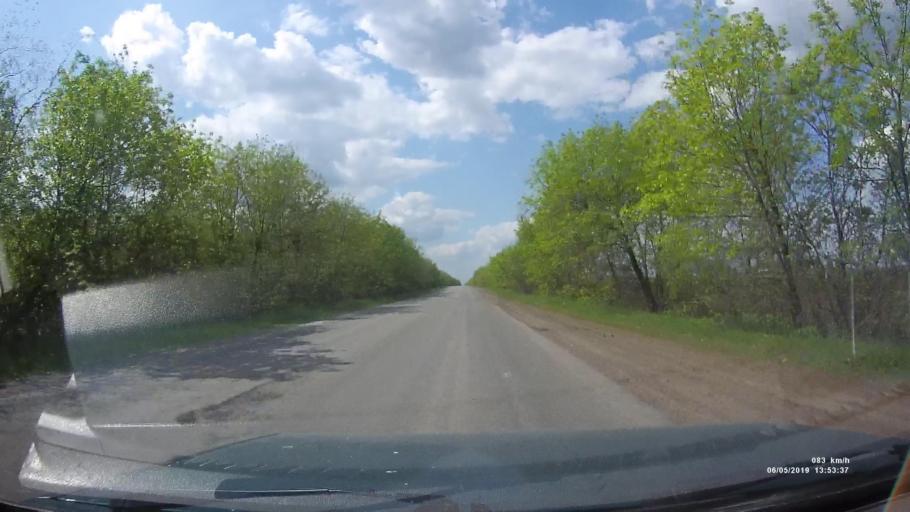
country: RU
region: Rostov
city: Melikhovskaya
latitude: 47.6693
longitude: 40.4597
